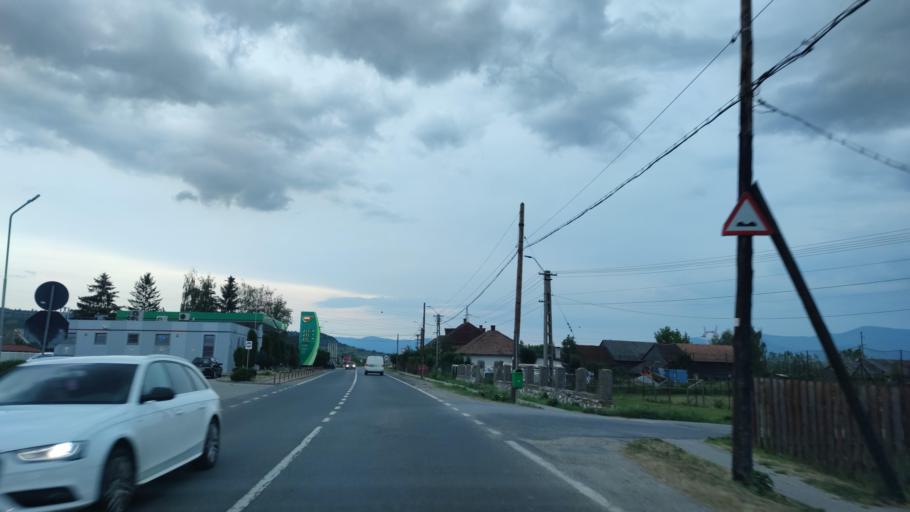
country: RO
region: Harghita
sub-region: Municipiul Gheorgheni
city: Gheorgheni
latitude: 46.7152
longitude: 25.6022
